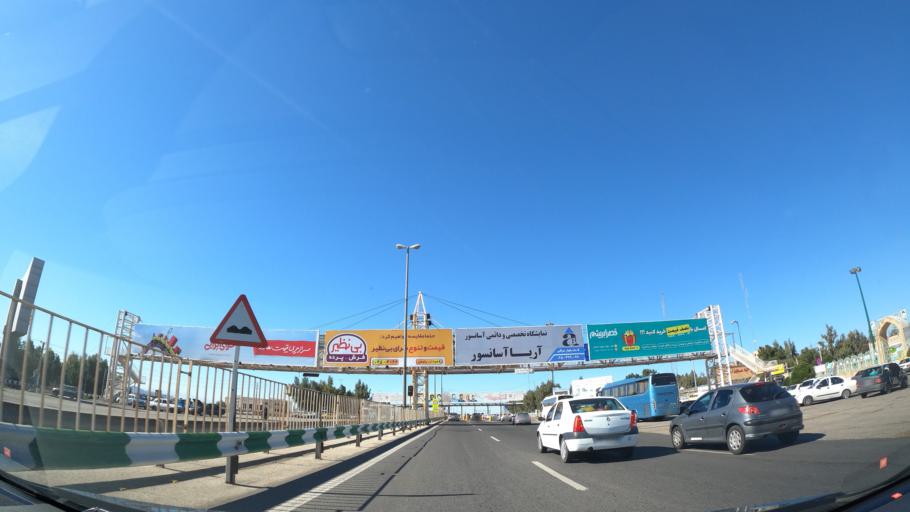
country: IR
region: Qom
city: Qom
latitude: 34.6847
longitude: 50.8918
